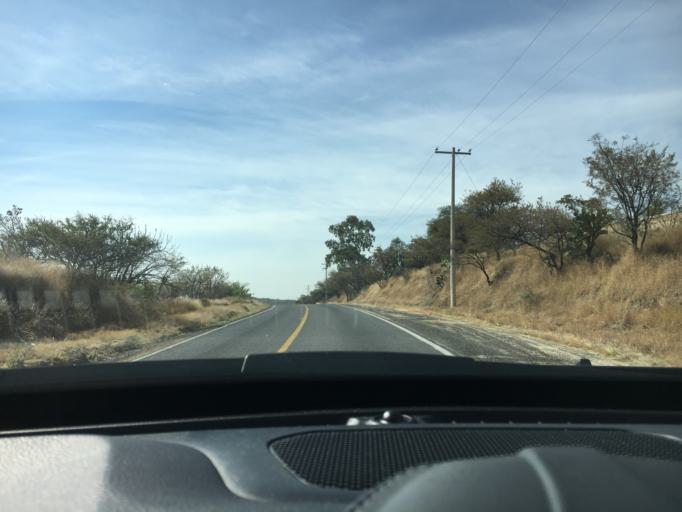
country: MX
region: Guanajuato
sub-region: Silao de la Victoria
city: San Francisco (Banos de Agua Caliente)
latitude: 21.0664
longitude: -101.4998
